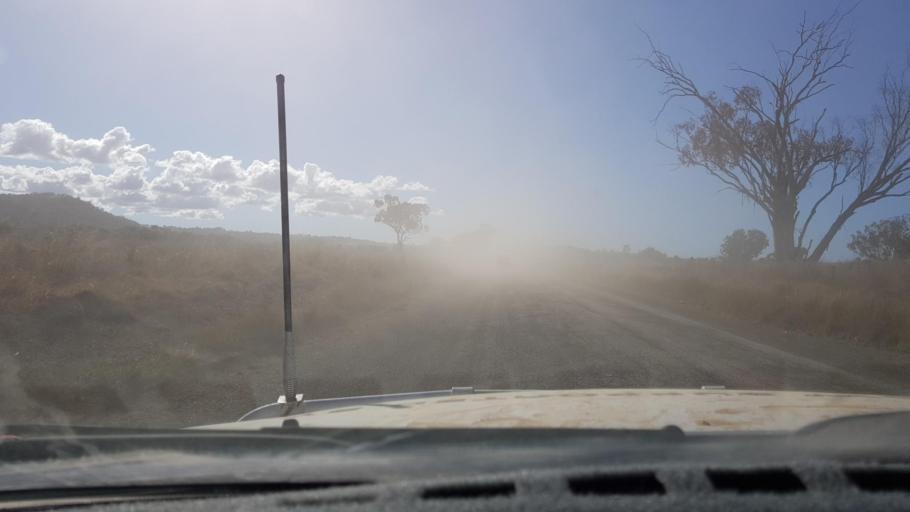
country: AU
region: New South Wales
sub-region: Narrabri
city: Blair Athol
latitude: -30.6716
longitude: 150.4529
